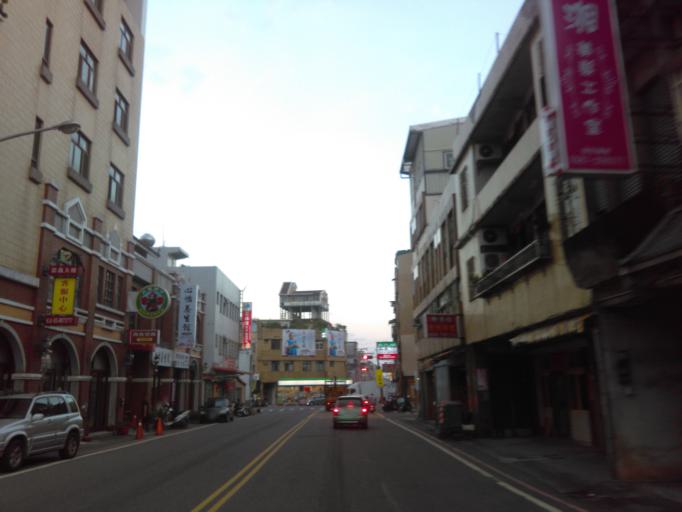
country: TW
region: Taiwan
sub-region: Yilan
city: Yilan
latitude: 24.8190
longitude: 121.7680
